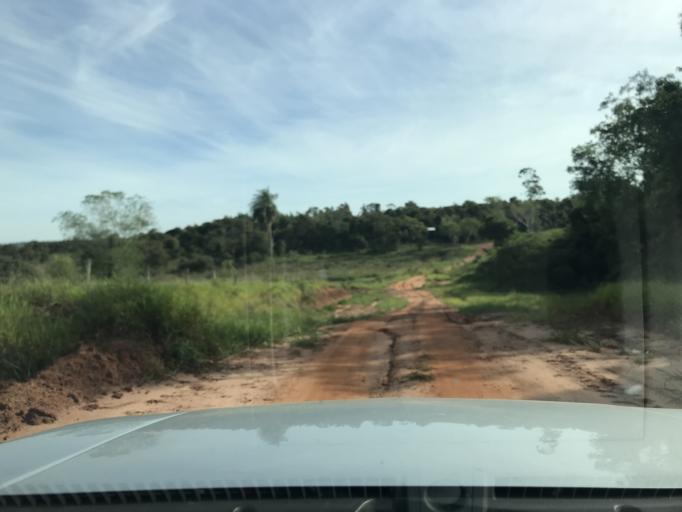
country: BR
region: Mato Grosso do Sul
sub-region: Iguatemi
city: Iguatemi
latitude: -23.6471
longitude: -54.5763
